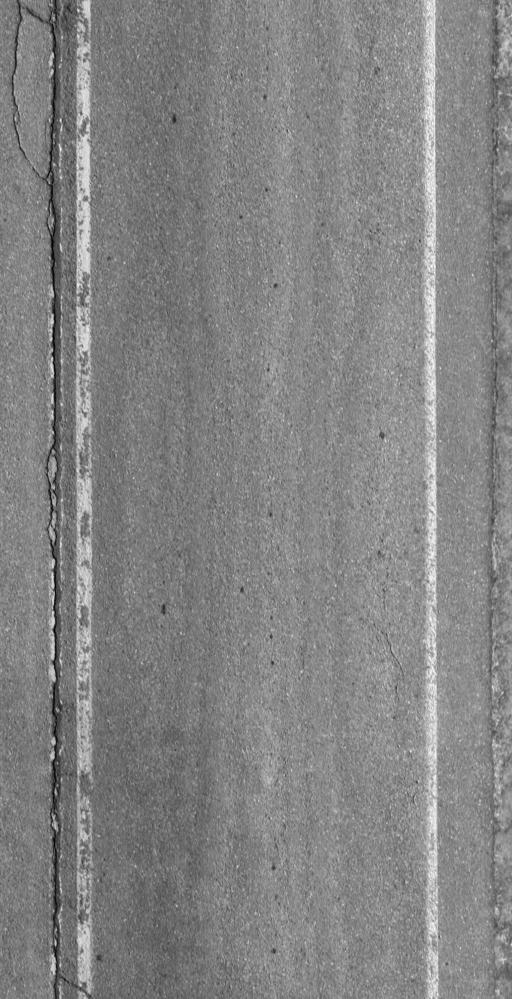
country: US
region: Vermont
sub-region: Chittenden County
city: Jericho
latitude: 44.4573
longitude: -73.0127
